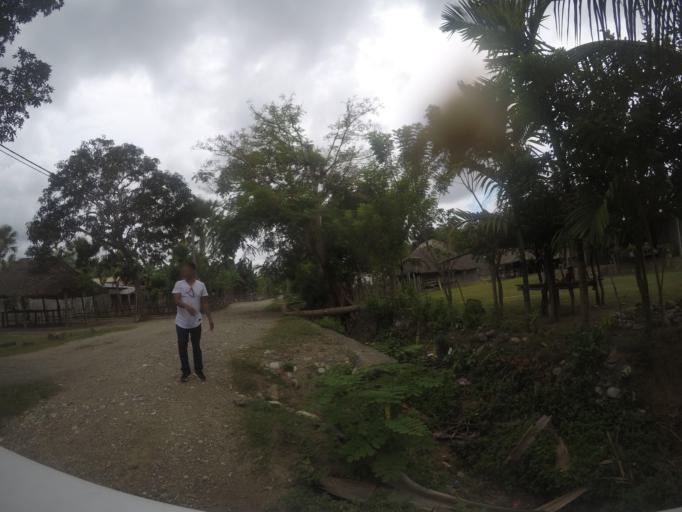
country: TL
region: Viqueque
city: Viqueque
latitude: -8.8796
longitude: 126.3651
